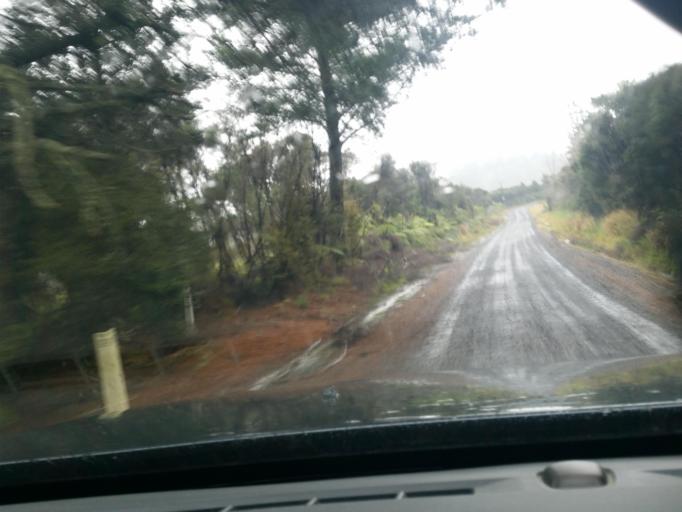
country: NZ
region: Northland
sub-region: Kaipara District
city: Dargaville
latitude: -35.7621
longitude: 173.6963
